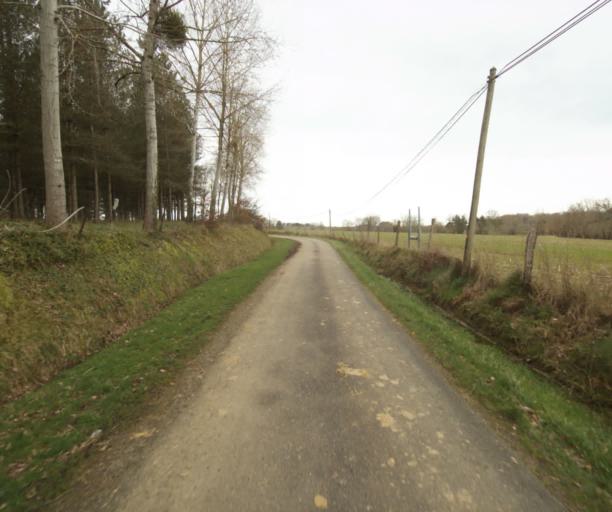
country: FR
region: Aquitaine
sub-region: Departement des Landes
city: Gabarret
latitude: 43.9362
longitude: 0.0270
